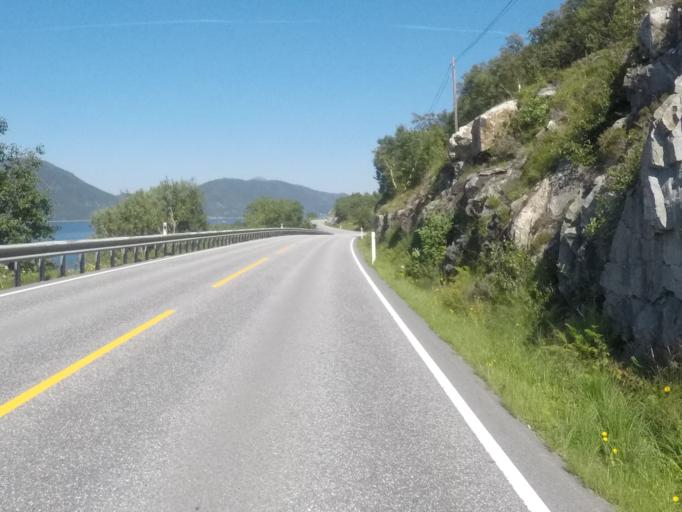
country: NO
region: More og Romsdal
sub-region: Hareid
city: Hareid
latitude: 62.2621
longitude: 5.9774
